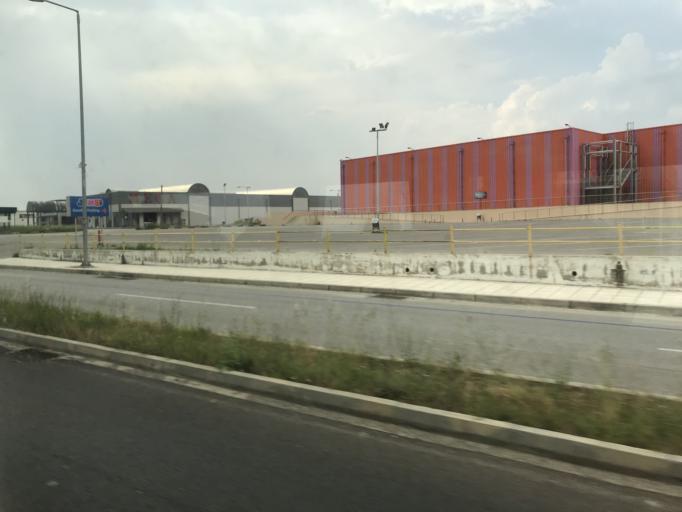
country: GR
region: East Macedonia and Thrace
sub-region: Nomos Evrou
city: Alexandroupoli
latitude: 40.8541
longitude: 25.9153
